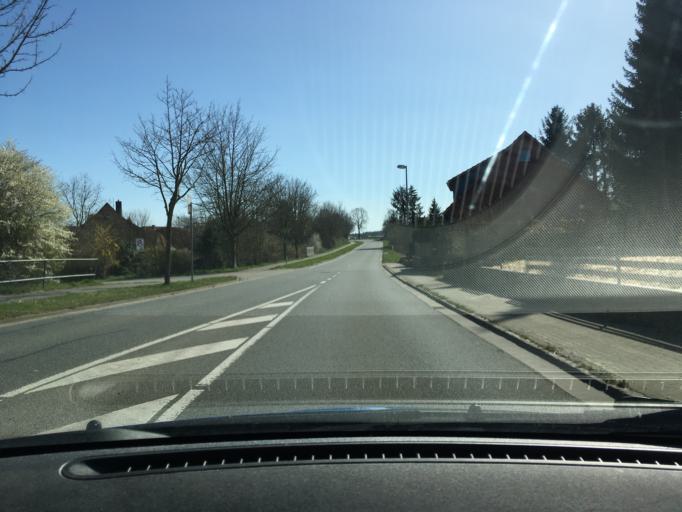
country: DE
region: Lower Saxony
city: Emmendorf
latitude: 53.0024
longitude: 10.5352
